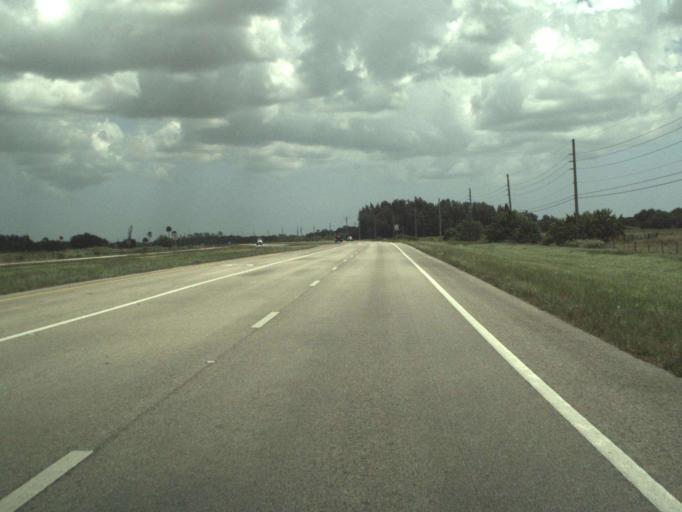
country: US
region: Florida
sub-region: Saint Lucie County
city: Fort Pierce South
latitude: 27.3857
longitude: -80.4658
